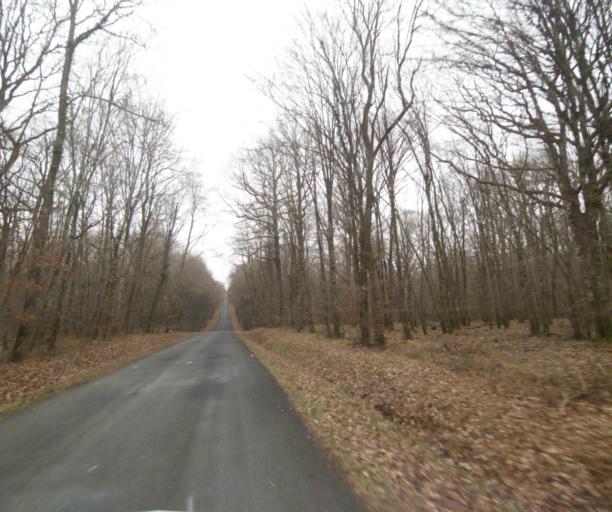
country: FR
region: Champagne-Ardenne
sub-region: Departement de la Haute-Marne
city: Bienville
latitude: 48.5567
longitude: 5.0027
